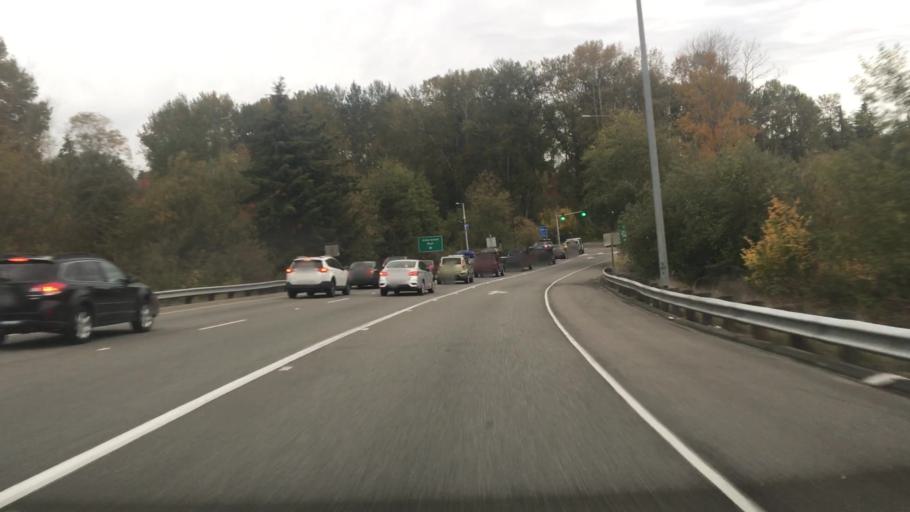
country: US
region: Washington
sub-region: Snohomish County
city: Alderwood Manor
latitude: 47.8123
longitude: -122.2940
